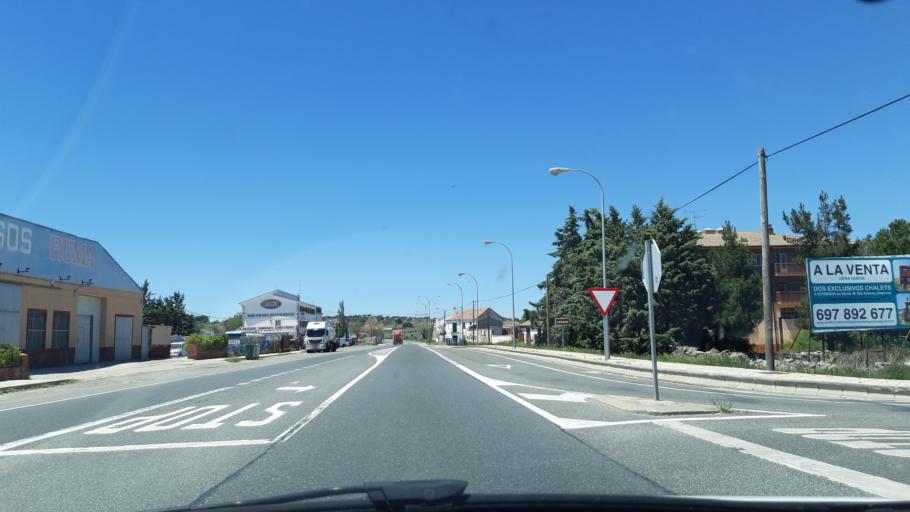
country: ES
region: Castille and Leon
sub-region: Provincia de Segovia
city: Zarzuela del Monte
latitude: 40.7570
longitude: -4.3299
